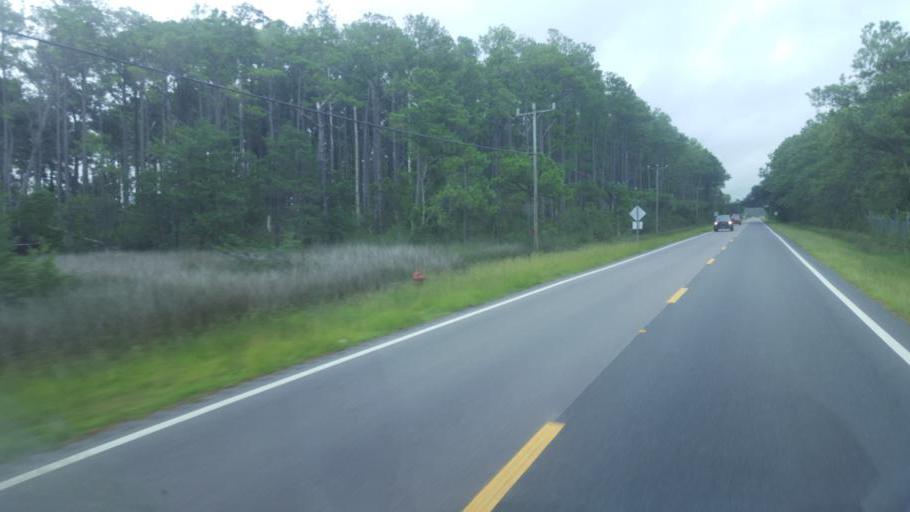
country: US
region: North Carolina
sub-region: Dare County
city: Wanchese
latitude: 35.8649
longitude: -75.6486
